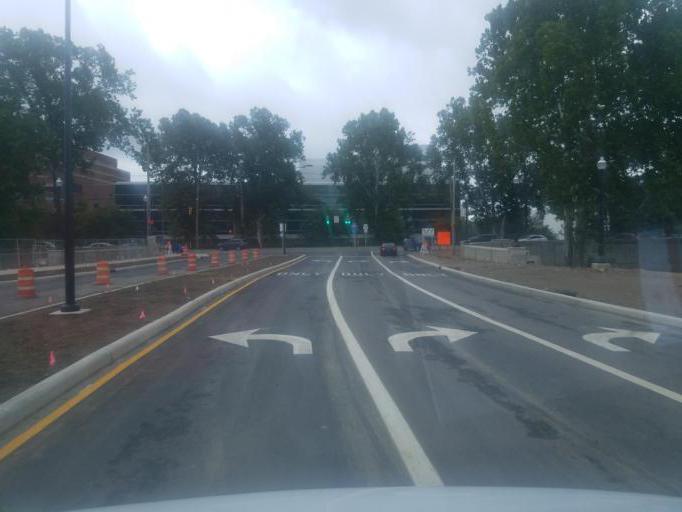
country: US
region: Ohio
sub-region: Franklin County
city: Grandview Heights
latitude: 39.9914
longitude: -83.0220
